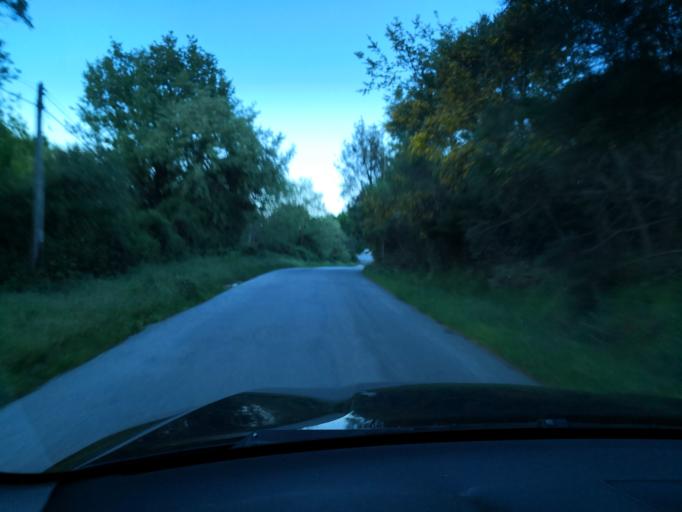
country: PT
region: Vila Real
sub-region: Vila Real
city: Vila Real
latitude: 41.3246
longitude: -7.7081
